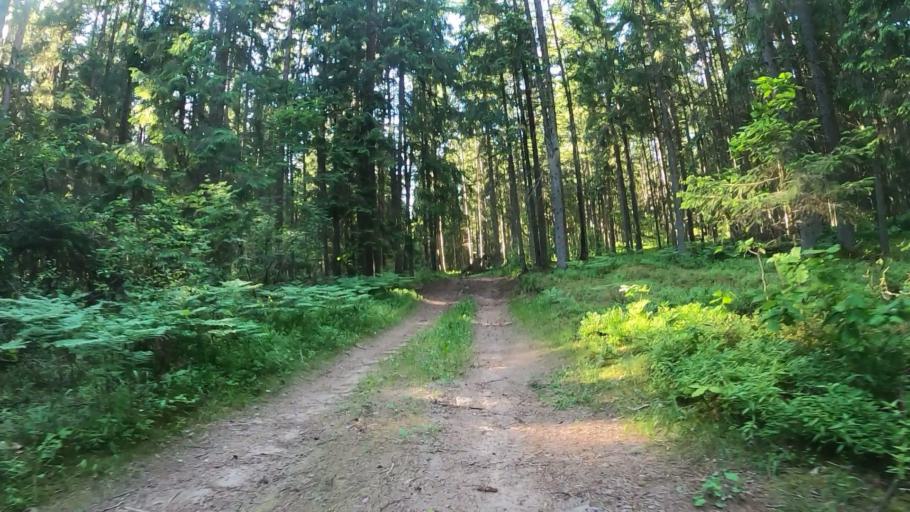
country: LV
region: Ogre
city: Ogre
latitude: 56.8311
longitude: 24.5962
